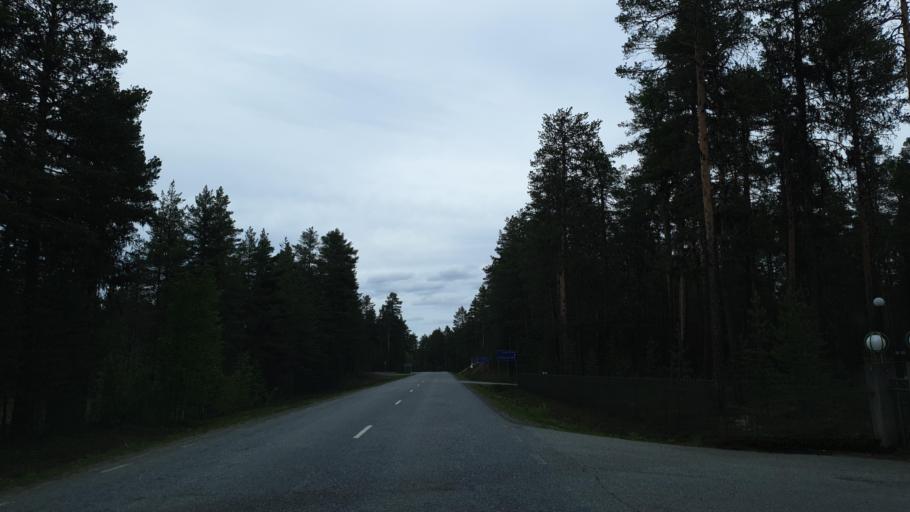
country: SE
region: Vaesterbotten
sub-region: Sorsele Kommun
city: Sorsele
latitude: 65.5480
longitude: 17.5085
